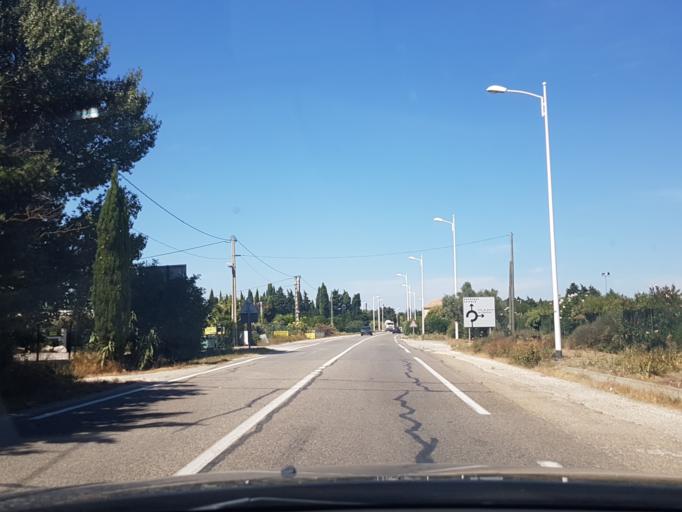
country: FR
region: Provence-Alpes-Cote d'Azur
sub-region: Departement des Bouches-du-Rhone
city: Rognonas
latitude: 43.8886
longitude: 4.8264
